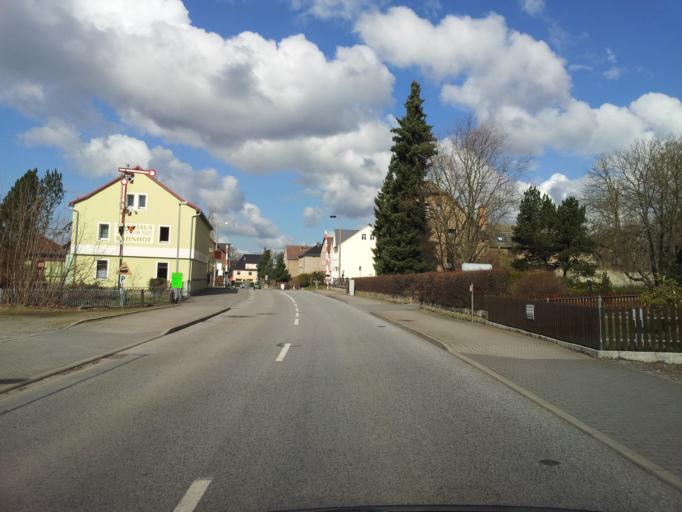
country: DE
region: Saxony
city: Ottendorf-Okrilla
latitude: 51.1868
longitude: 13.8376
